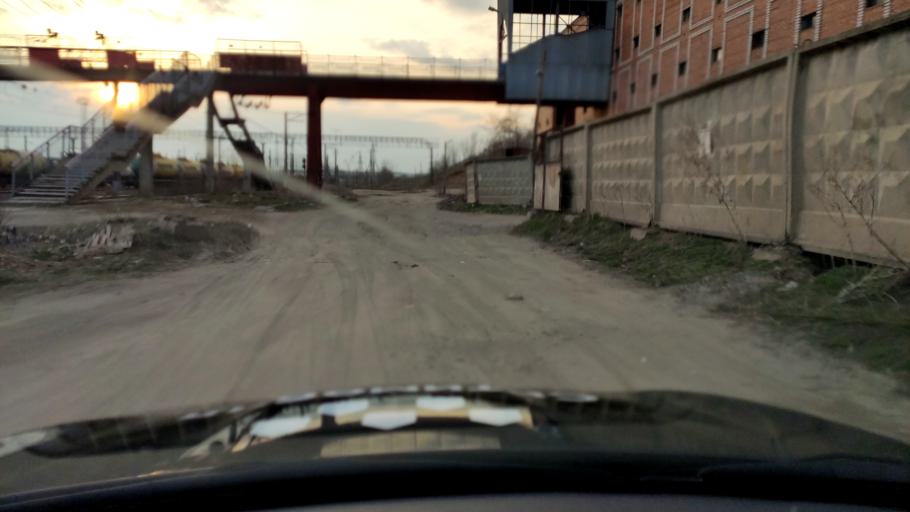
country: RU
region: Samara
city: Zhigulevsk
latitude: 53.4789
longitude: 49.5262
